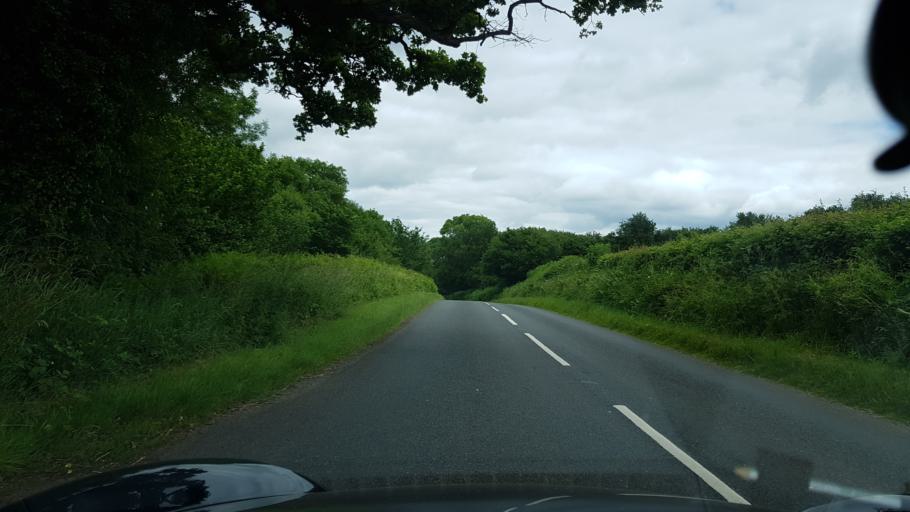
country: GB
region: England
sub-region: Herefordshire
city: Llanrothal
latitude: 51.8711
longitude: -2.8254
